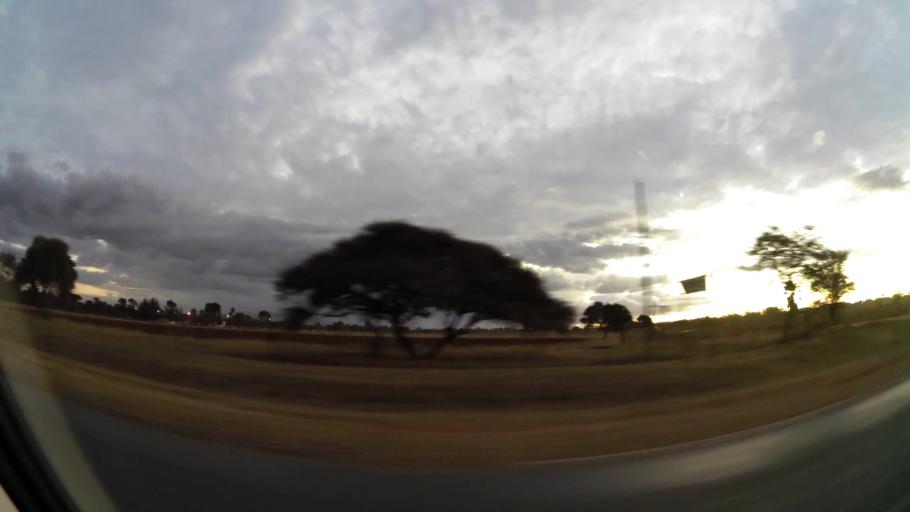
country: ZA
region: Limpopo
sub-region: Capricorn District Municipality
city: Polokwane
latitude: -23.8199
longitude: 29.4253
